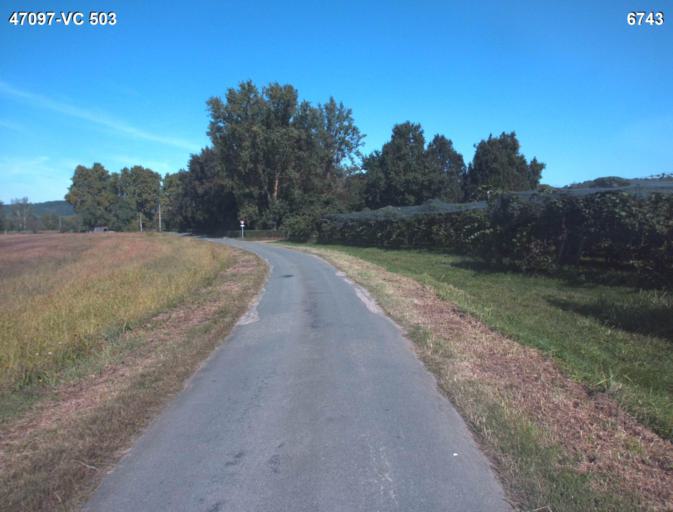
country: FR
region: Aquitaine
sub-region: Departement du Lot-et-Garonne
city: Port-Sainte-Marie
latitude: 44.2420
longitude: 0.3841
